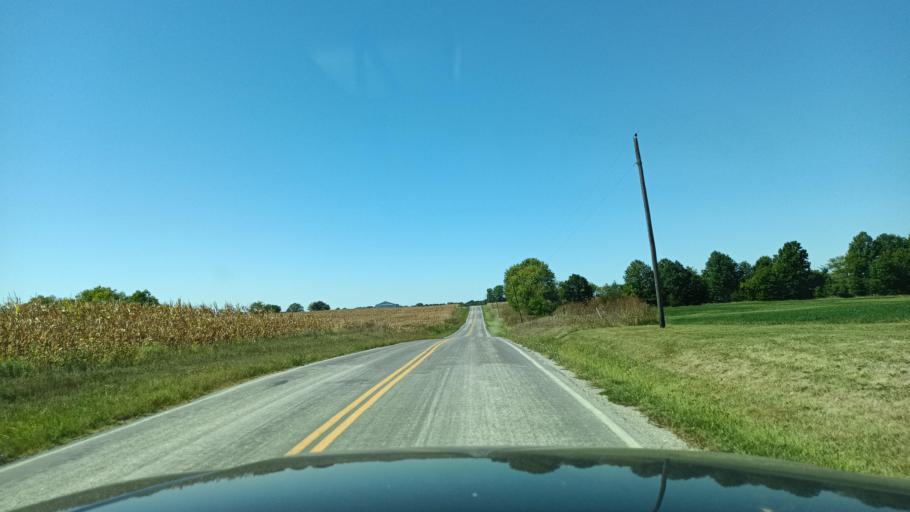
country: US
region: Missouri
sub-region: Macon County
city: La Plata
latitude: 40.0228
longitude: -92.5736
